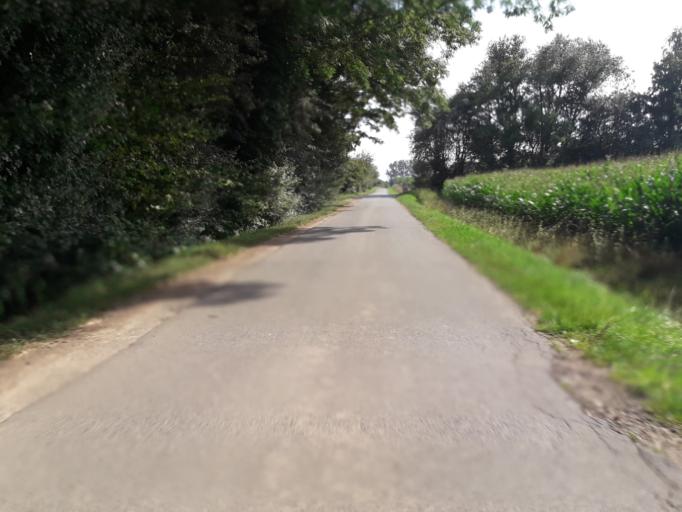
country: DE
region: North Rhine-Westphalia
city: Bad Lippspringe
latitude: 51.7604
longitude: 8.8033
